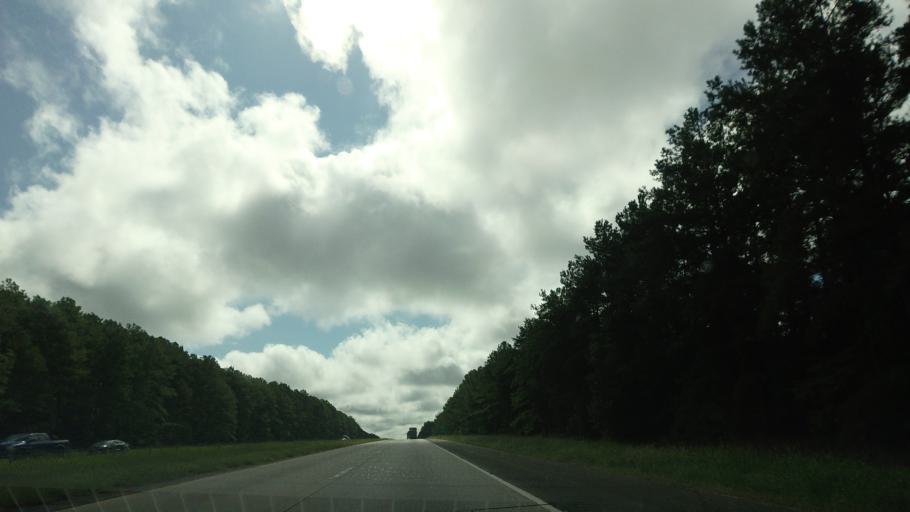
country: US
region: Georgia
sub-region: Twiggs County
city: Jeffersonville
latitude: 32.6689
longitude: -83.4671
